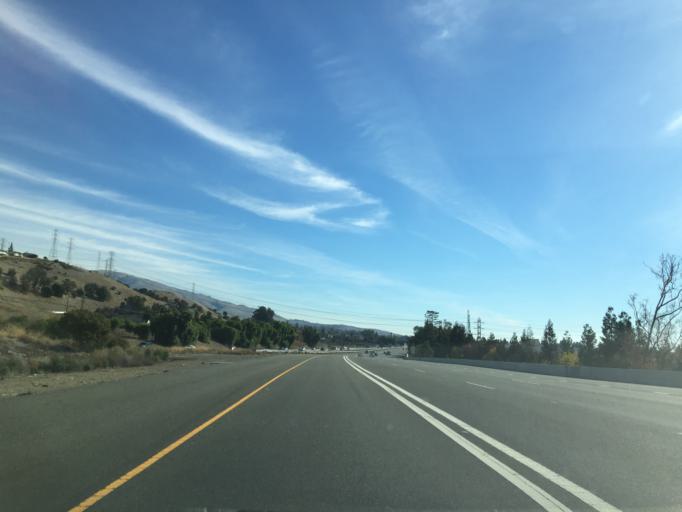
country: US
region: California
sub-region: Alameda County
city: Fremont
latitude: 37.5218
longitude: -121.9450
